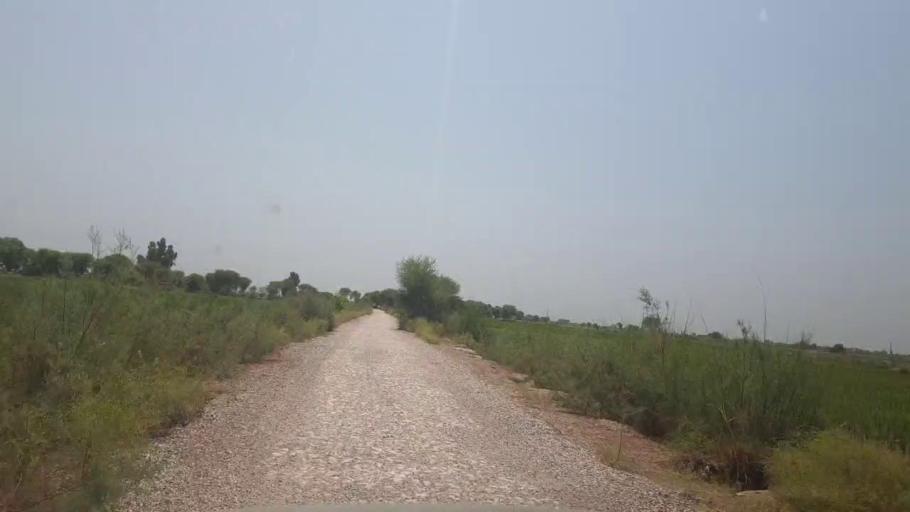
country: PK
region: Sindh
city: Lakhi
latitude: 27.8498
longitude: 68.6650
